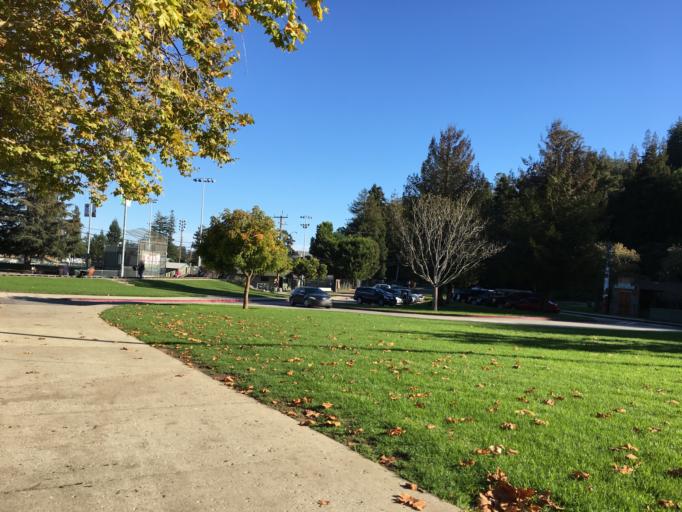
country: US
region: California
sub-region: Santa Cruz County
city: Santa Cruz
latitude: 36.9841
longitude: -122.0383
